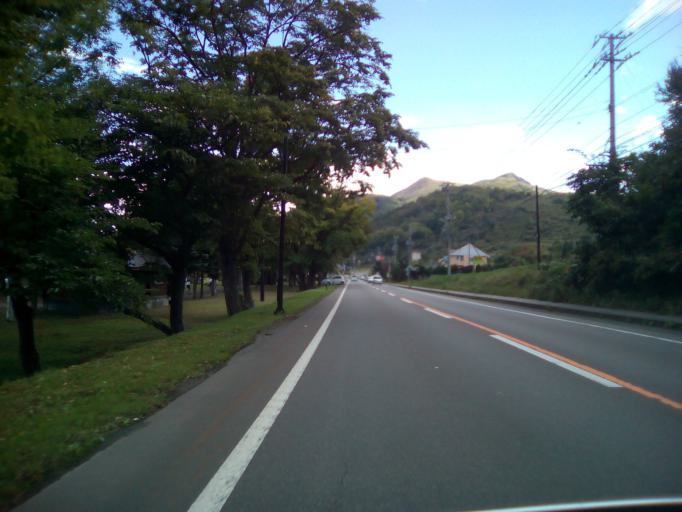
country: JP
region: Hokkaido
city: Date
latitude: 42.5666
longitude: 140.8071
